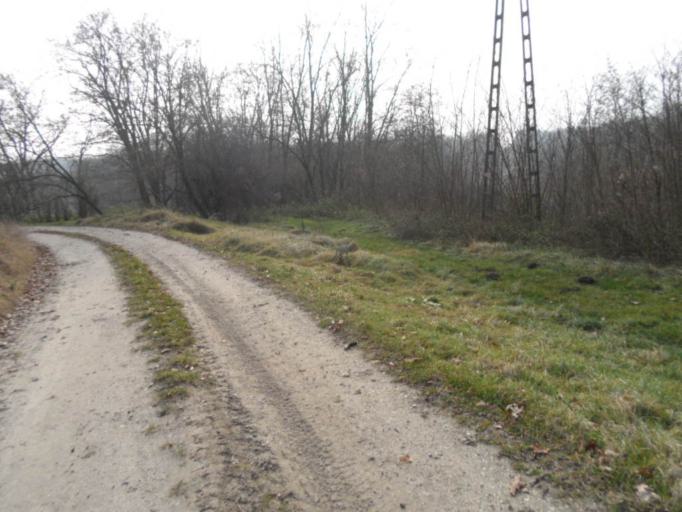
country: HU
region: Somogy
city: Siofok
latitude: 46.8440
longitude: 18.0200
